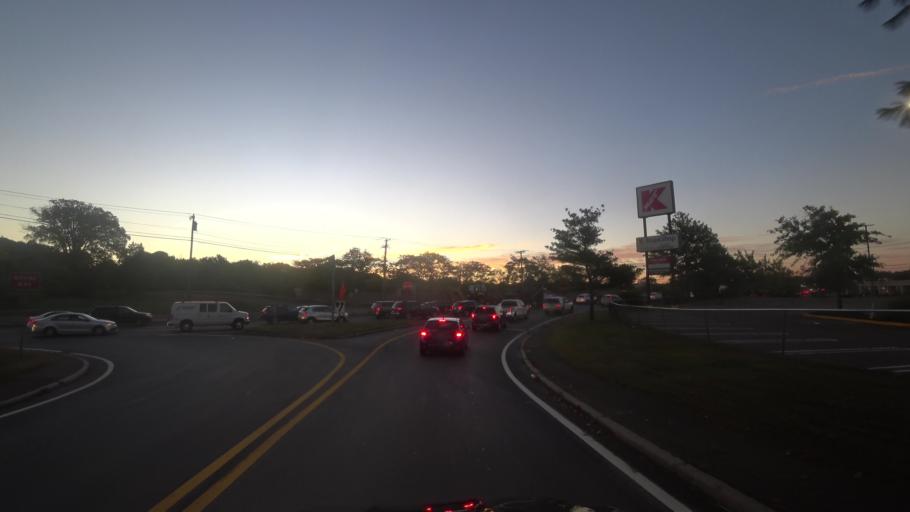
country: US
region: Massachusetts
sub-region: Essex County
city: Saugus
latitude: 42.4645
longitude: -71.0255
